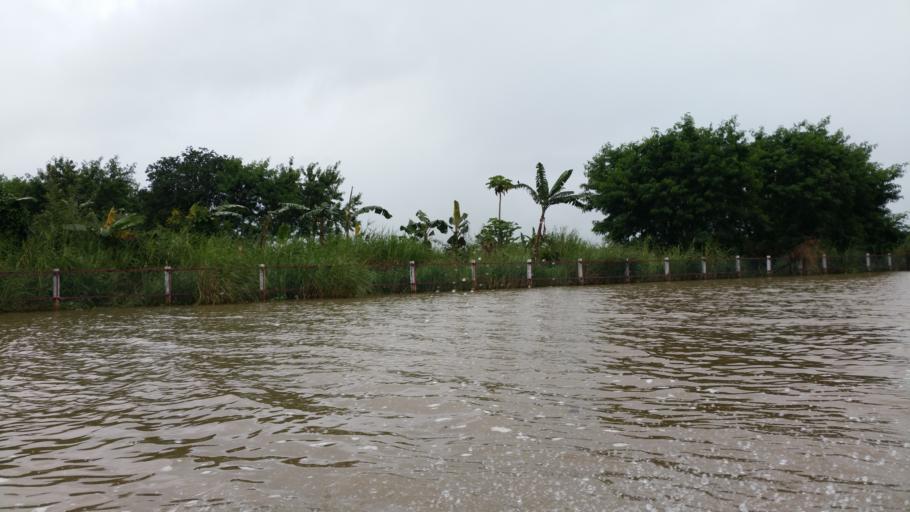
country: MM
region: Shan
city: Taunggyi
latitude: 20.6350
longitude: 96.9213
